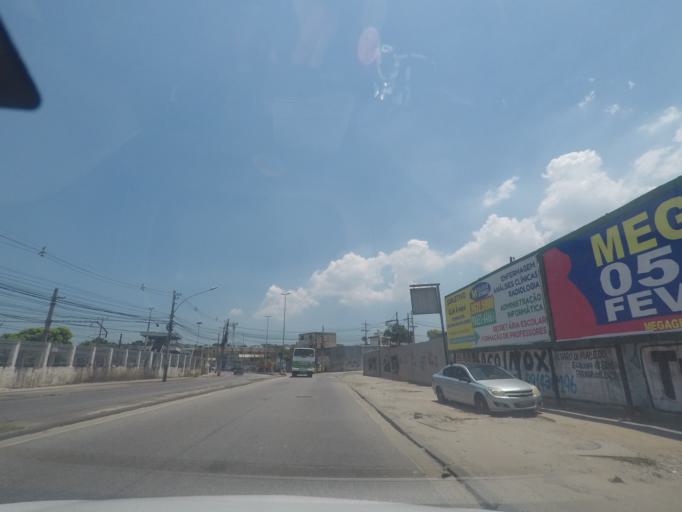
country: BR
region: Rio de Janeiro
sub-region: Duque De Caxias
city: Duque de Caxias
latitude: -22.8047
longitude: -43.3057
